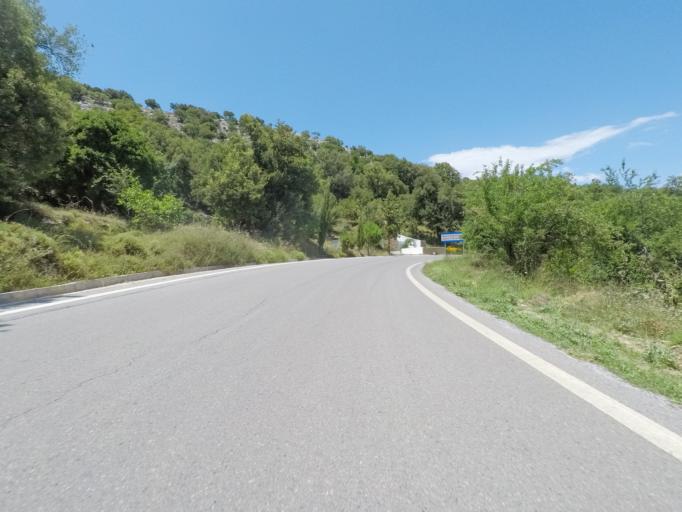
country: GR
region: Crete
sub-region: Nomos Irakleiou
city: Mokhos
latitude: 35.1734
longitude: 25.4366
